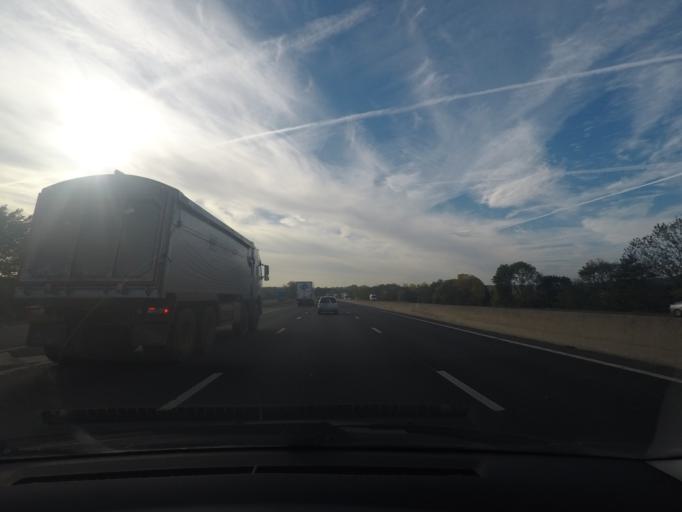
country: GB
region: England
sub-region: Barnsley
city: Darton
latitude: 53.6074
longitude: -1.5521
